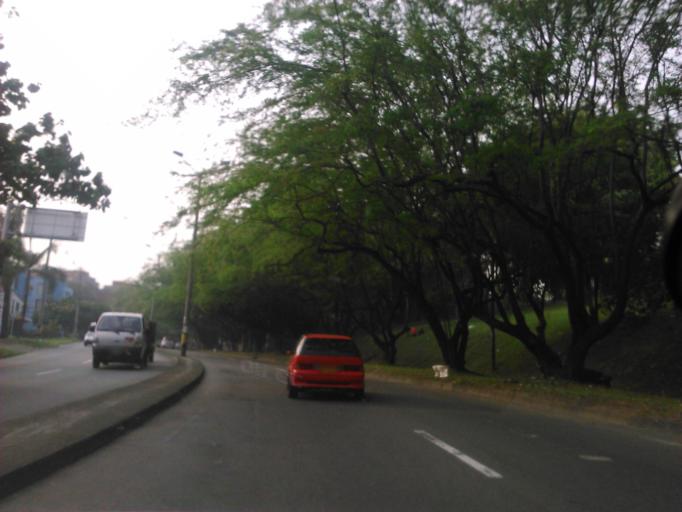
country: CO
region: Antioquia
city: Medellin
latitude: 6.2370
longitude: -75.6031
